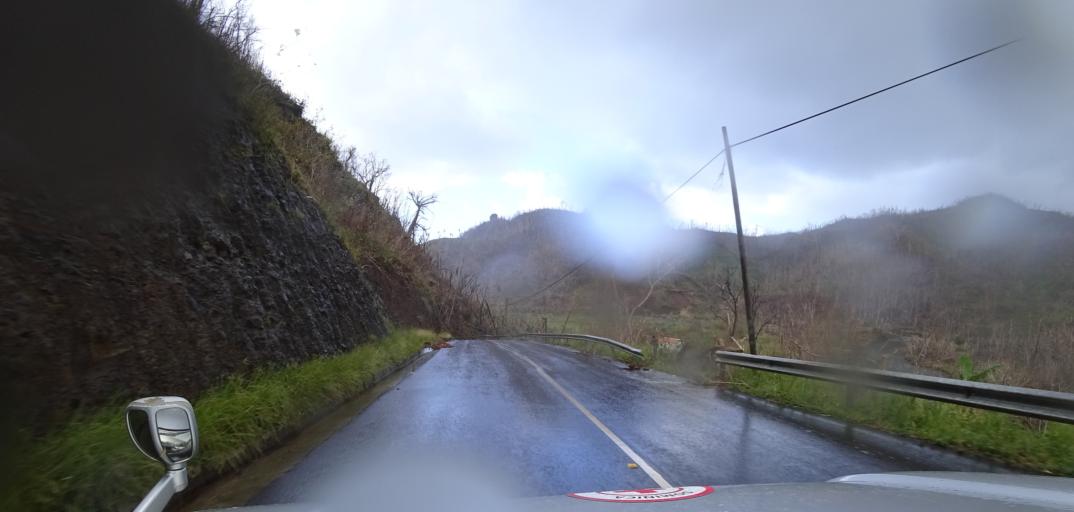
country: DM
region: Saint Andrew
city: Marigot
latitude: 15.5115
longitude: -61.2797
